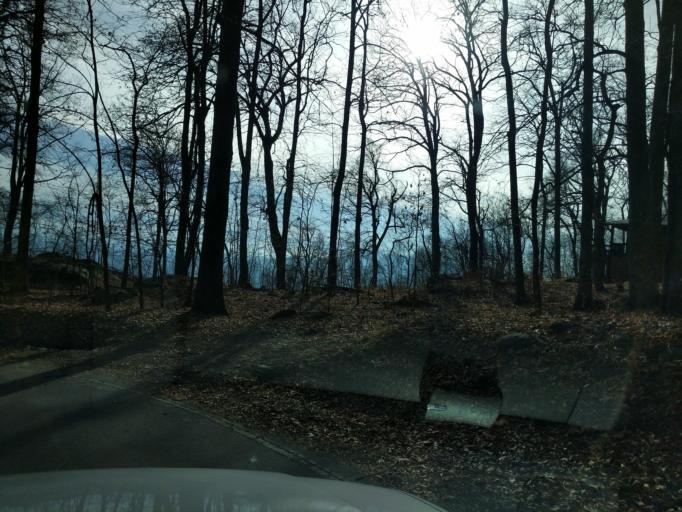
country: US
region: North Carolina
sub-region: Polk County
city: Columbus
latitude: 35.2720
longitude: -82.2209
